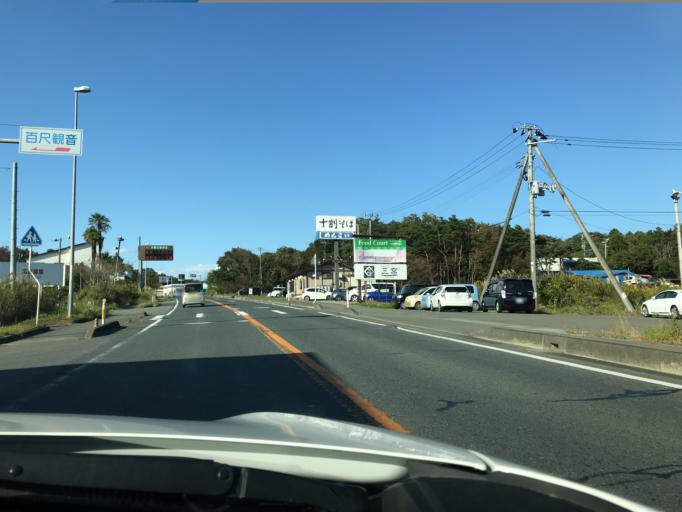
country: JP
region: Miyagi
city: Marumori
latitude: 37.7725
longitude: 140.9434
